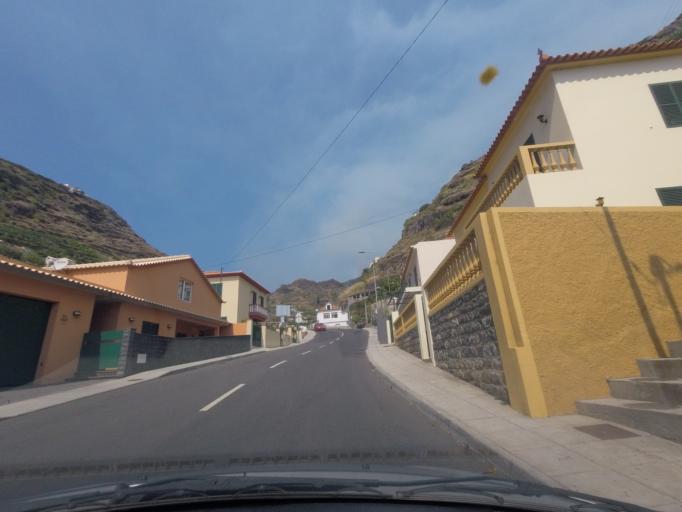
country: PT
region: Madeira
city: Ponta do Sol
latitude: 32.6785
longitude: -17.0778
